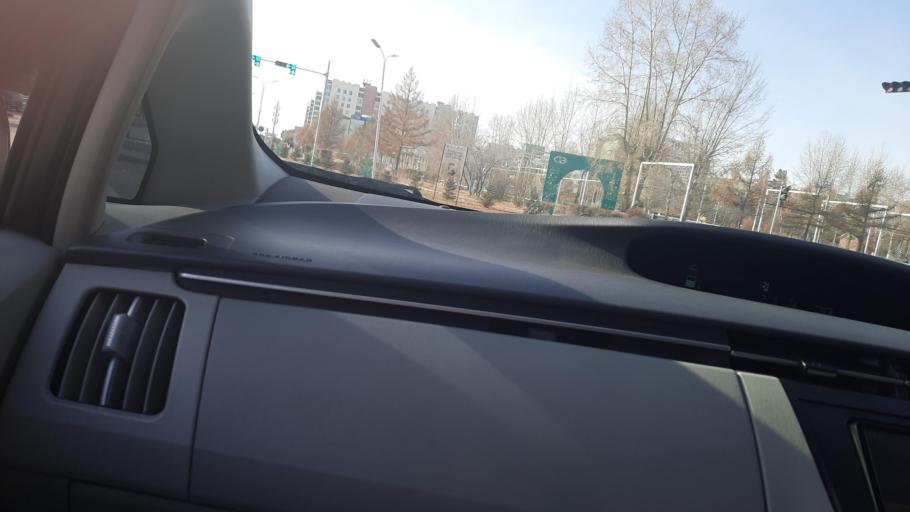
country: MN
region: Orhon
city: Erdenet
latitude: 49.0308
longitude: 104.0558
